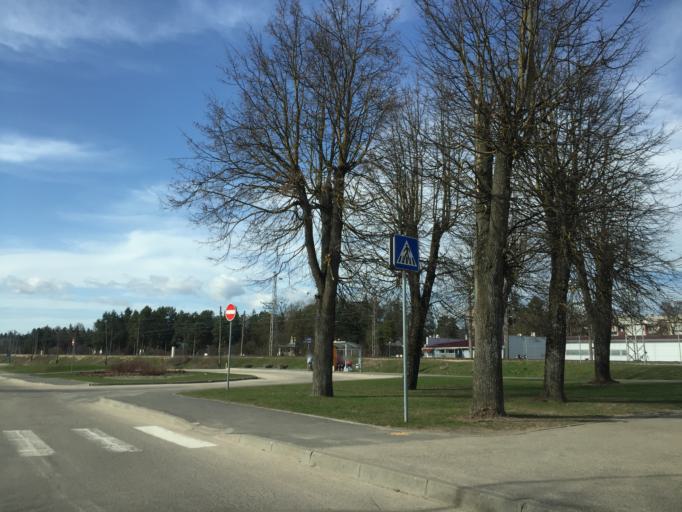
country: LV
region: Ogre
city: Ogre
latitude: 56.8184
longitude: 24.5926
